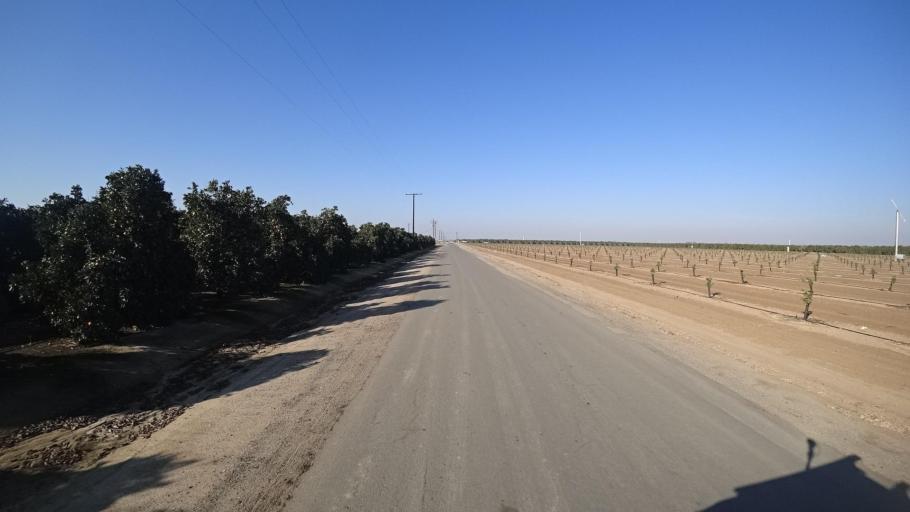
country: US
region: California
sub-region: Tulare County
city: Richgrove
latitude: 35.7253
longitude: -119.1455
